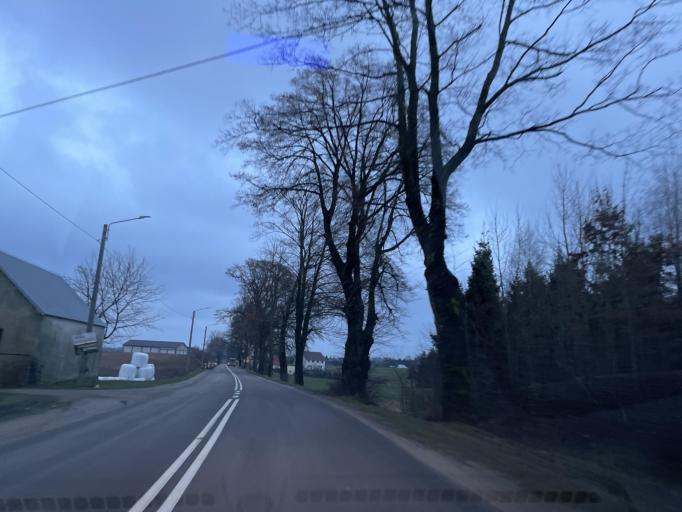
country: PL
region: Pomeranian Voivodeship
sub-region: Powiat kartuski
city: Przodkowo
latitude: 54.4021
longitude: 18.2202
